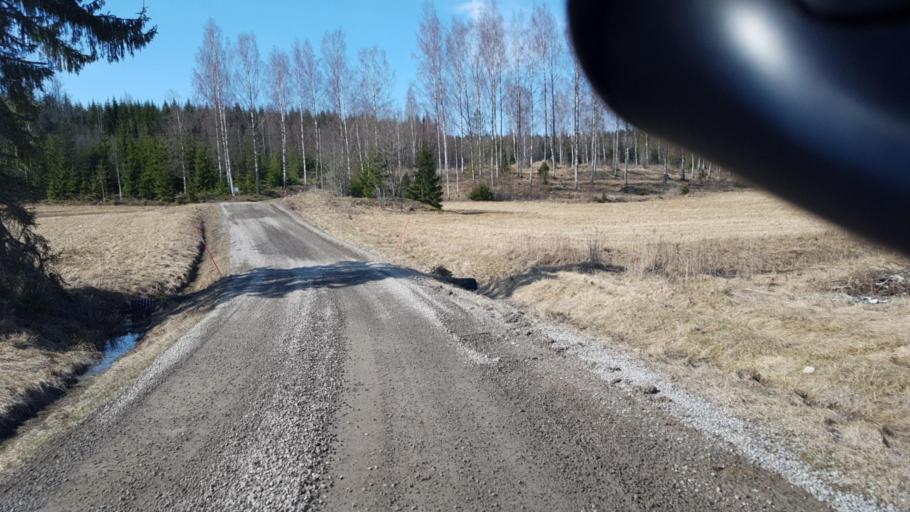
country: SE
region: Vaermland
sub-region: Arvika Kommun
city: Arvika
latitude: 59.5527
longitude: 12.8496
